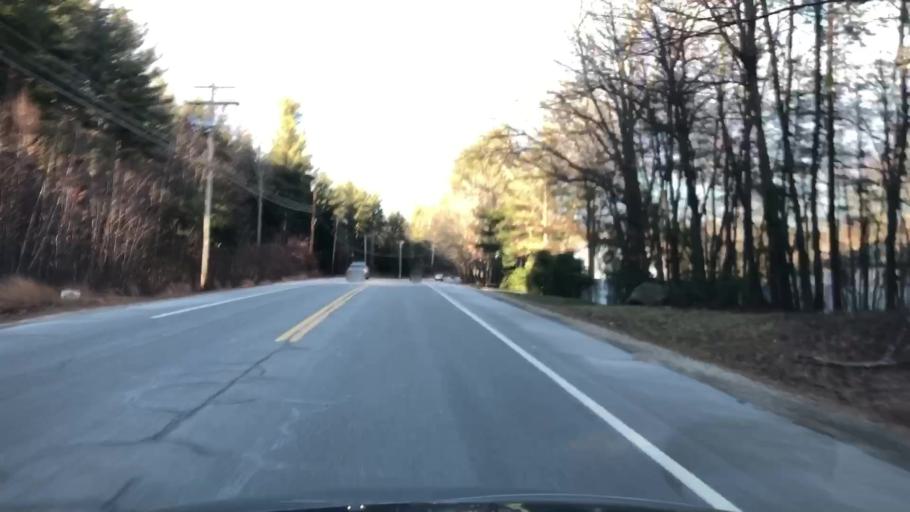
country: US
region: New Hampshire
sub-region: Hillsborough County
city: Milford
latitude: 42.7871
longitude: -71.6589
